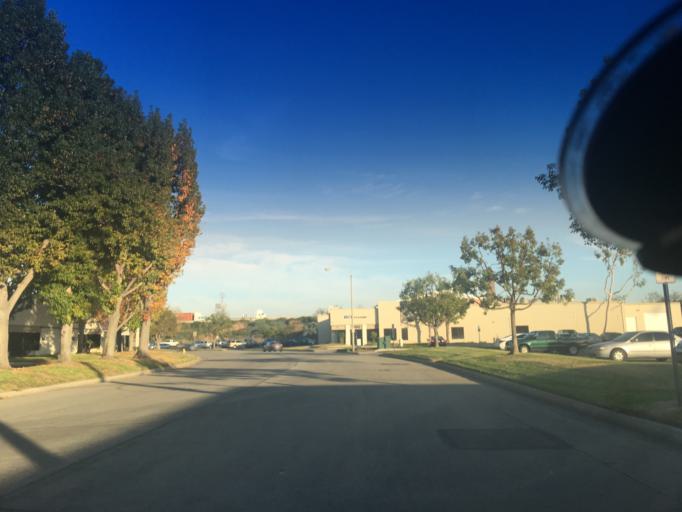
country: US
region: California
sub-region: Orange County
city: Orange
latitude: 33.8083
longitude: -117.8819
